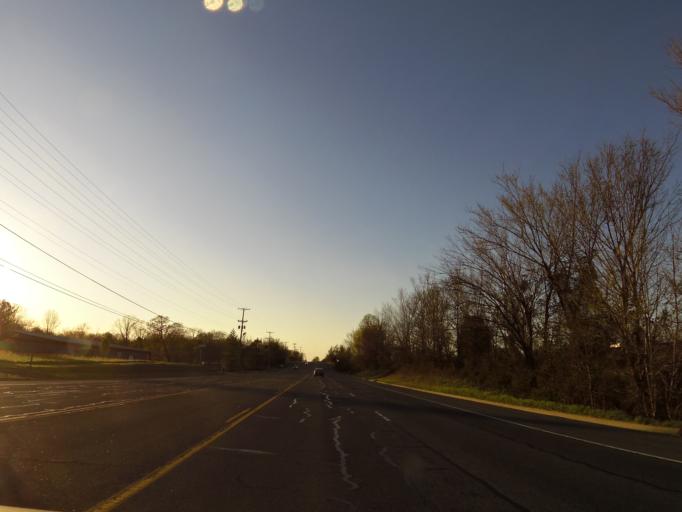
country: US
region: Tennessee
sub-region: Robertson County
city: Greenbrier
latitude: 36.4673
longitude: -86.8416
